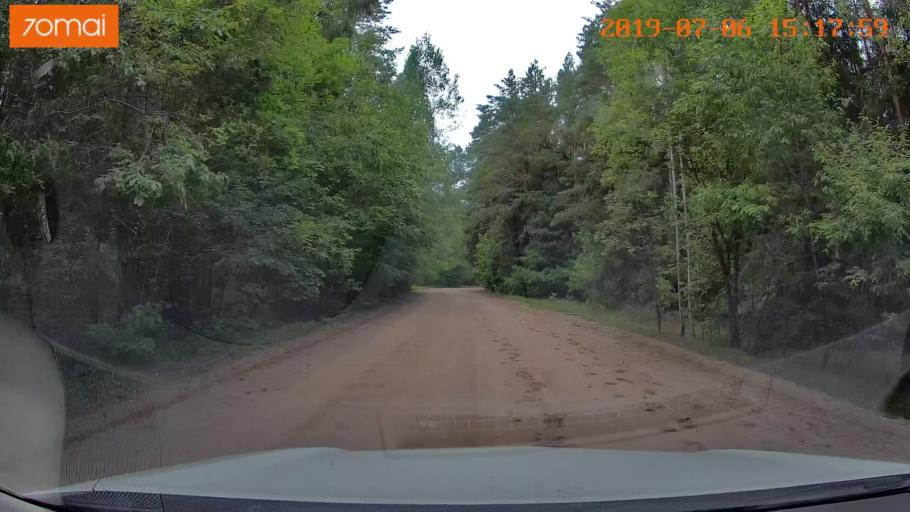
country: BY
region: Minsk
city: Ivyanyets
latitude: 53.9912
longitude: 26.6571
